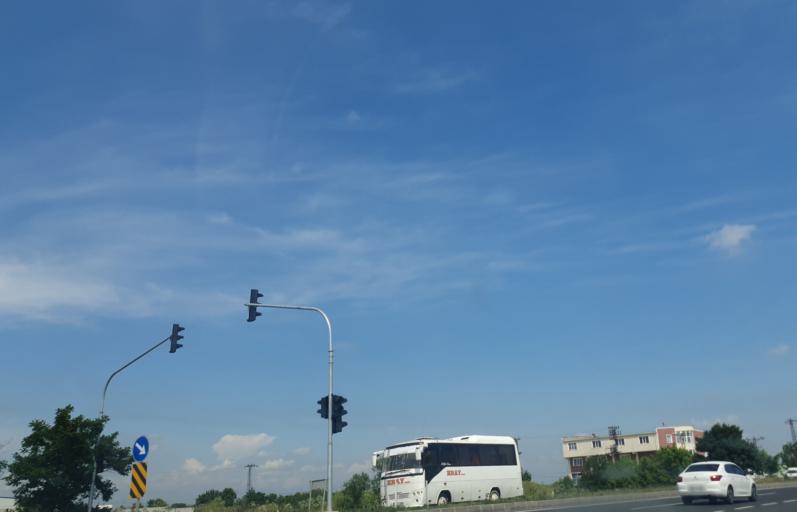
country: TR
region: Tekirdag
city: Beyazkoy
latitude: 41.2649
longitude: 27.6524
